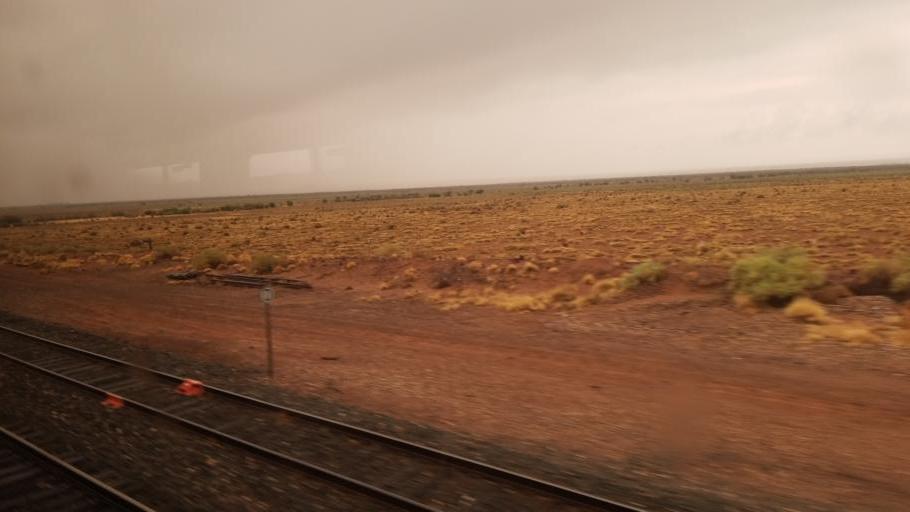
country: US
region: Arizona
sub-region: Navajo County
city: Joseph City
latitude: 34.9676
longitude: -110.5091
